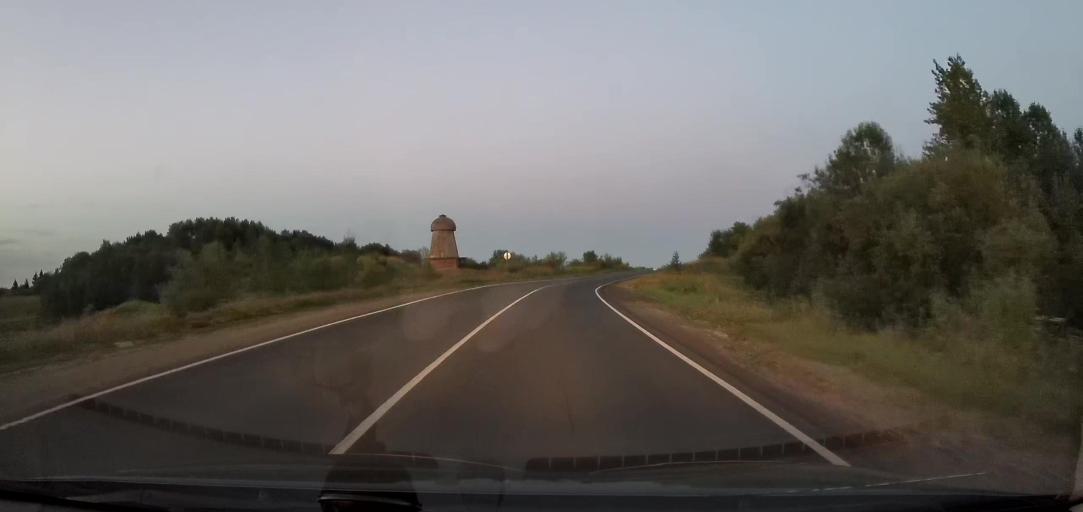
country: RU
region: Arkhangelskaya
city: Uyemskiy
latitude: 64.4500
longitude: 40.9436
